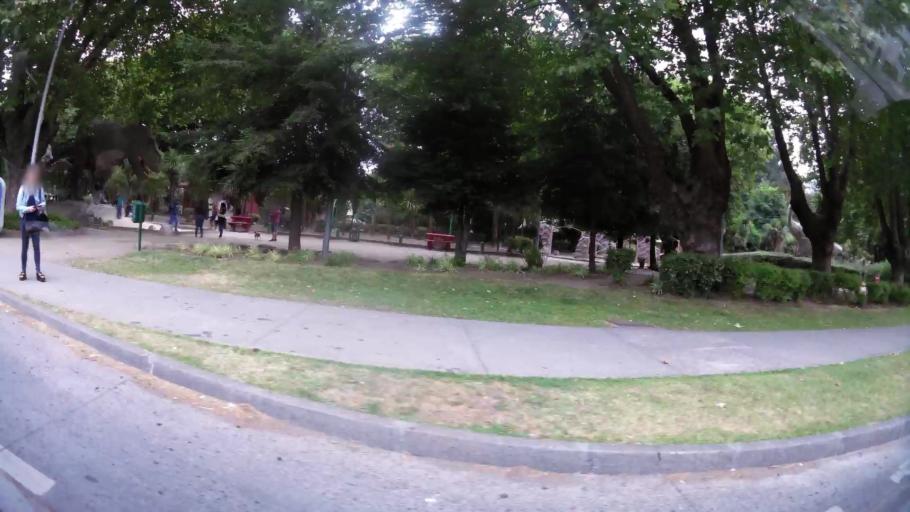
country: CL
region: Biobio
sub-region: Provincia de Concepcion
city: Concepcion
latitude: -36.8153
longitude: -73.0313
